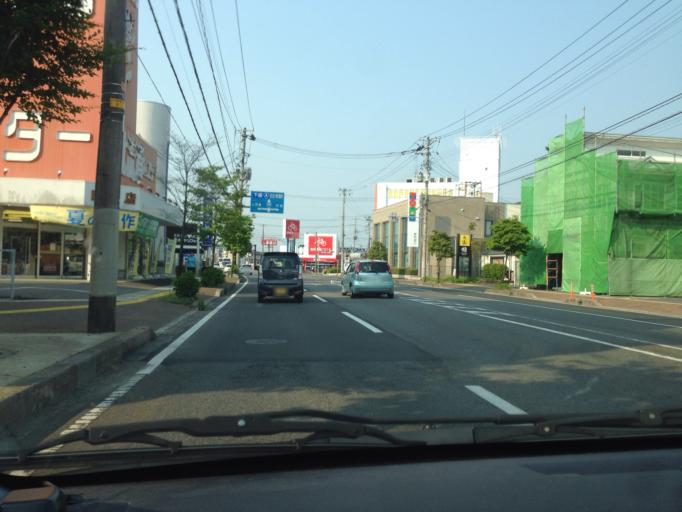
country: JP
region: Tochigi
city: Kuroiso
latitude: 37.1246
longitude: 140.1963
